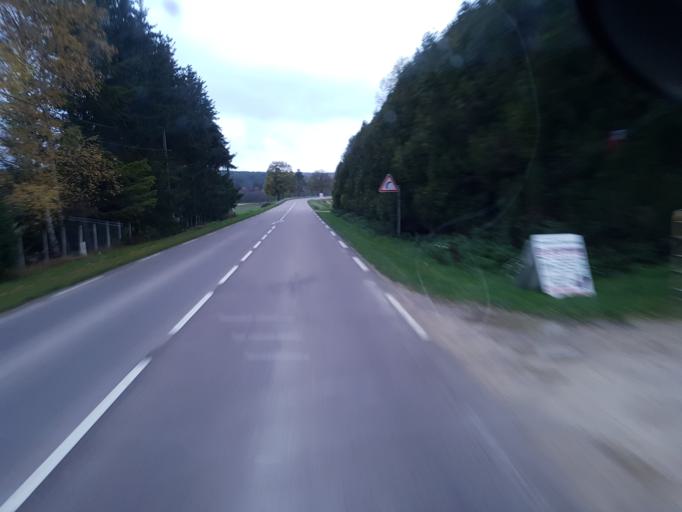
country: FR
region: Champagne-Ardenne
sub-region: Departement de l'Aube
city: Mussy-sur-Seine
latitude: 47.9853
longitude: 4.4892
